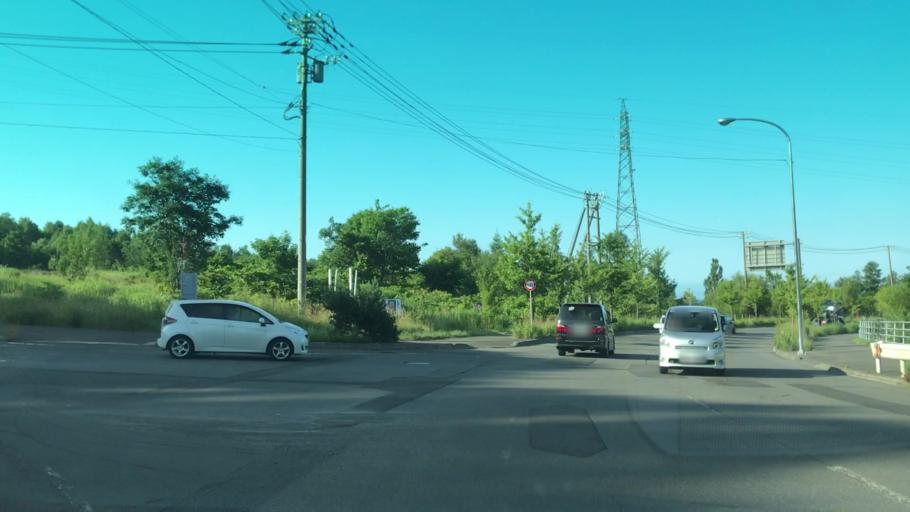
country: JP
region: Hokkaido
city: Otaru
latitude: 43.1663
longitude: 141.0460
